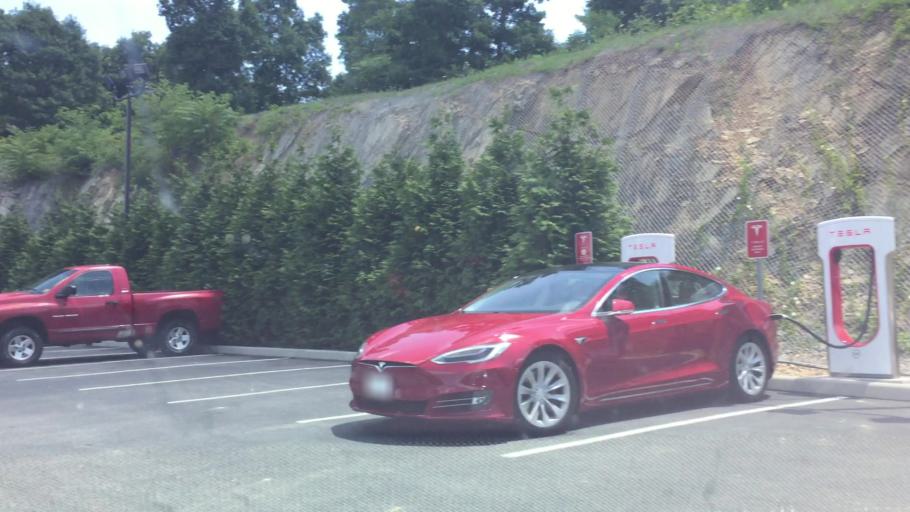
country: US
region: Virginia
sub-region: Wythe County
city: Wytheville
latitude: 36.9457
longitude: -81.0547
